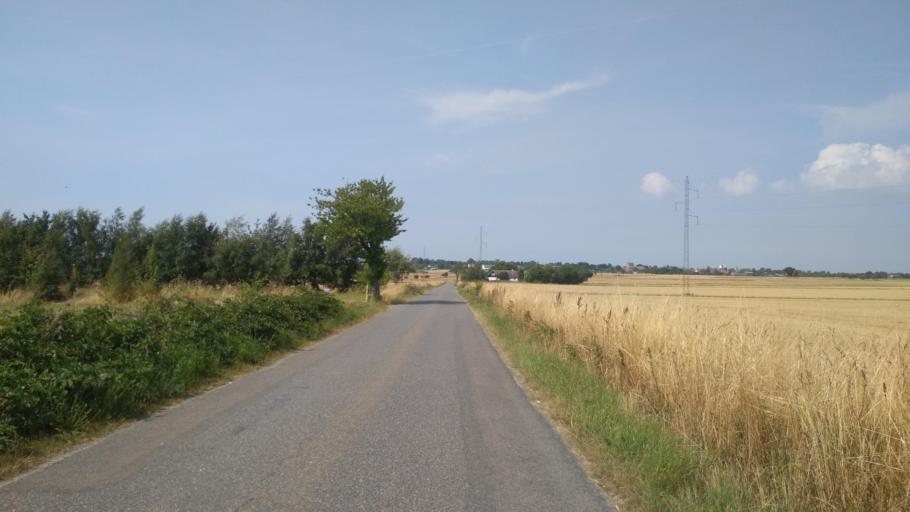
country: DK
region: Capital Region
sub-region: Bornholm Kommune
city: Akirkeby
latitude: 55.0620
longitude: 14.9452
